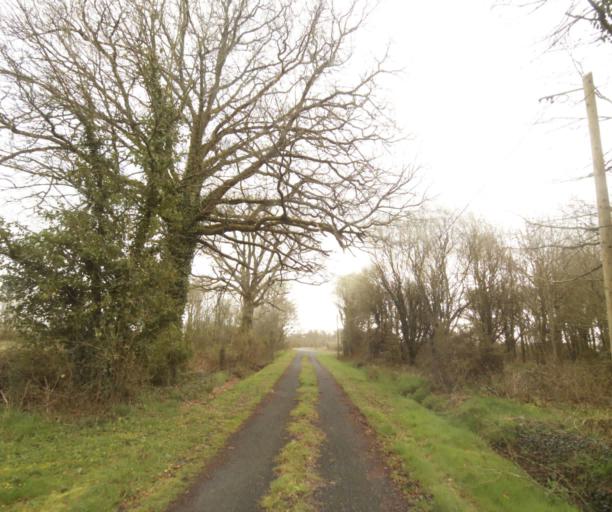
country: FR
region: Pays de la Loire
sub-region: Departement de la Loire-Atlantique
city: Bouvron
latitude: 47.3975
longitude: -1.8727
